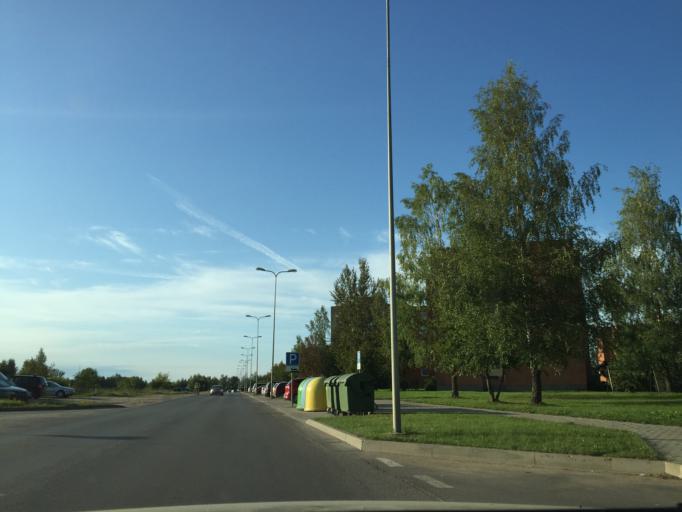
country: LT
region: Panevezys
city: Rokiskis
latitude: 55.9466
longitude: 25.5799
